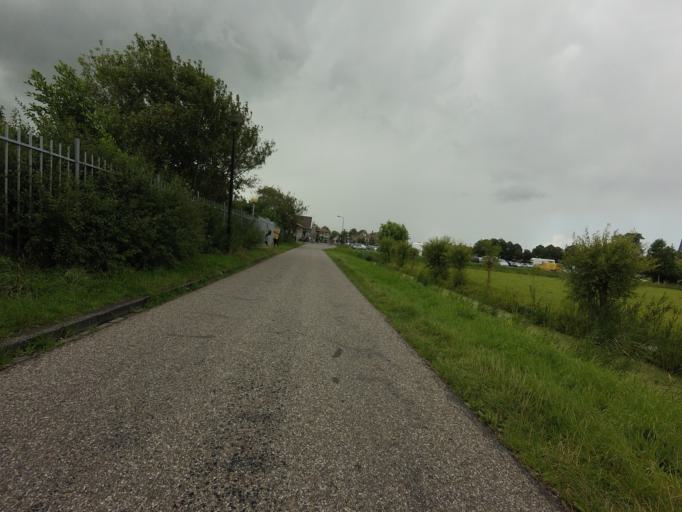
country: NL
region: Friesland
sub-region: Gemeente Franekeradeel
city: Franeker
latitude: 53.1887
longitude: 5.5506
